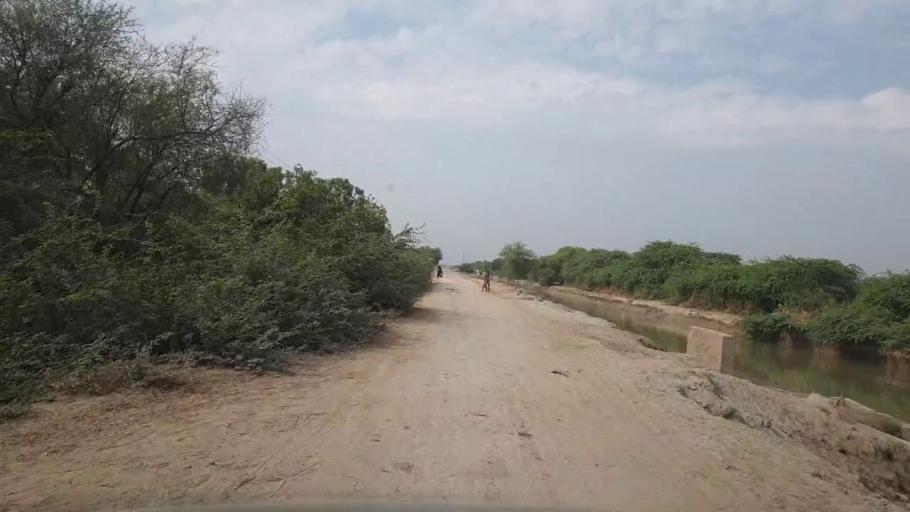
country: PK
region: Sindh
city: Kario
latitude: 24.6313
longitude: 68.5712
